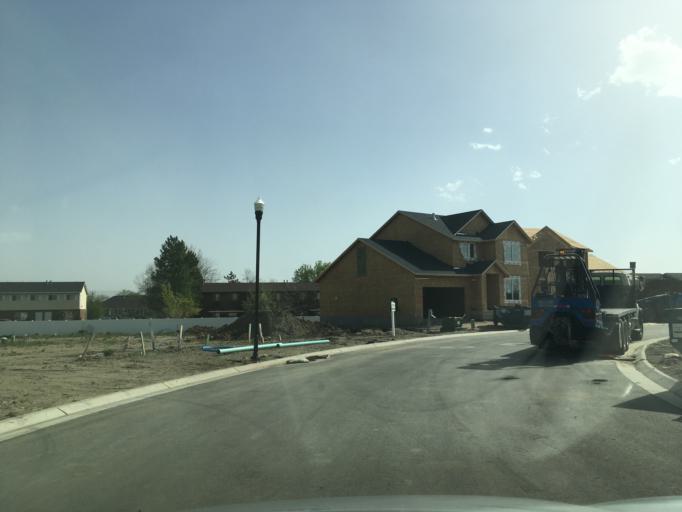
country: US
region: Utah
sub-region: Davis County
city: Farmington
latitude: 40.9711
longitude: -111.8895
